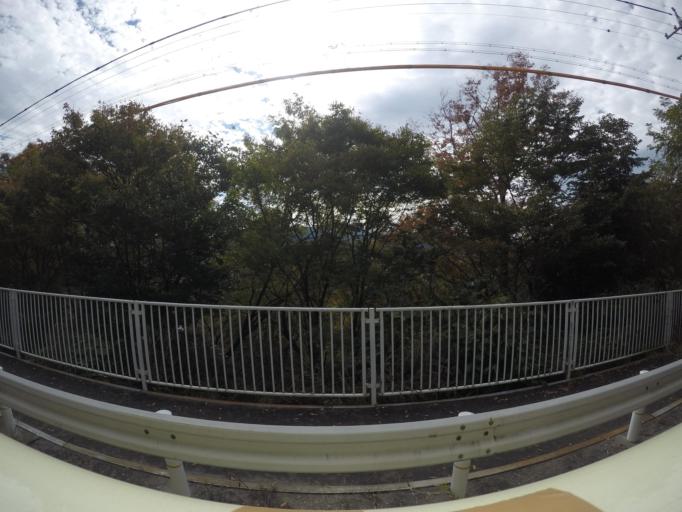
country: JP
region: Nagano
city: Ina
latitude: 35.8391
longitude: 138.0504
